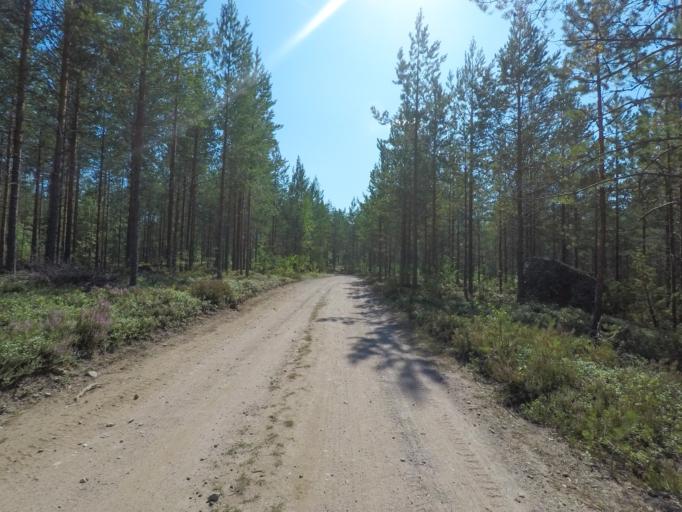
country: FI
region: Southern Savonia
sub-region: Mikkeli
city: Puumala
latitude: 61.4286
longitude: 28.0069
